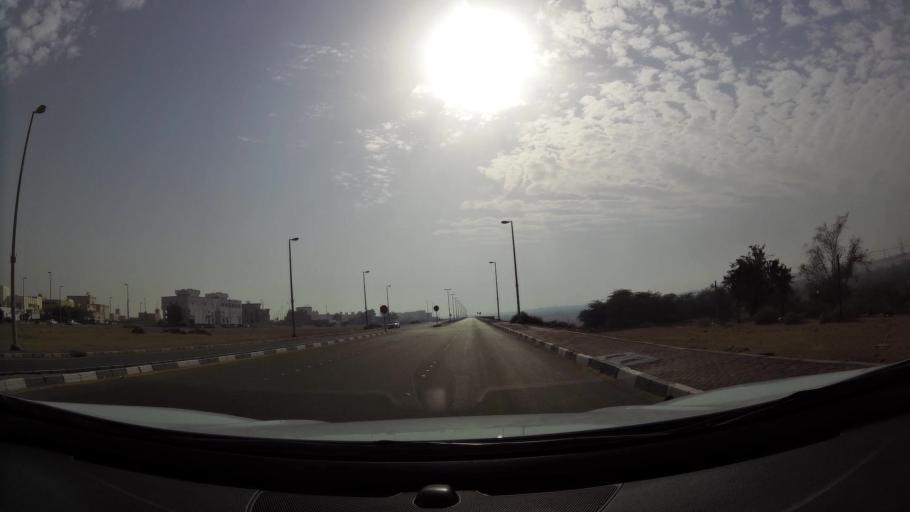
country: AE
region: Abu Dhabi
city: Abu Dhabi
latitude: 24.2540
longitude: 54.7161
